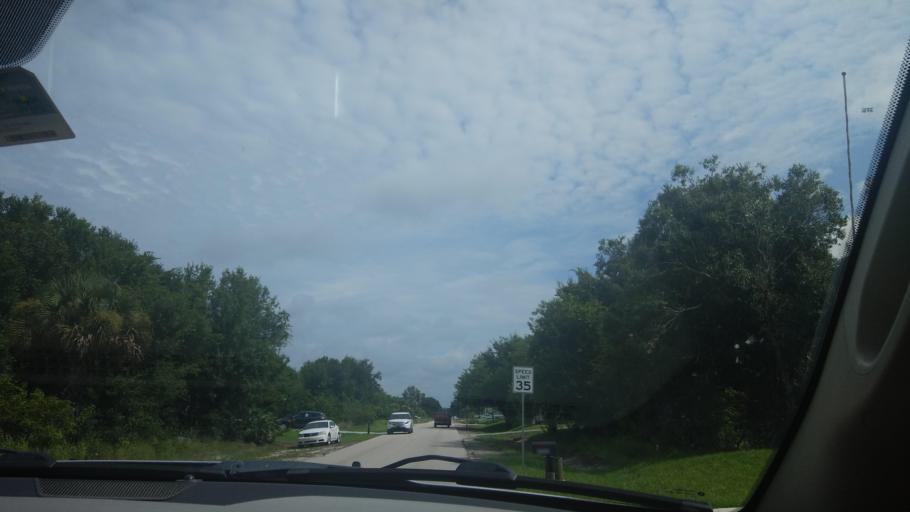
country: US
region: Florida
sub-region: Indian River County
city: Fellsmere
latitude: 27.7589
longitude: -80.5338
